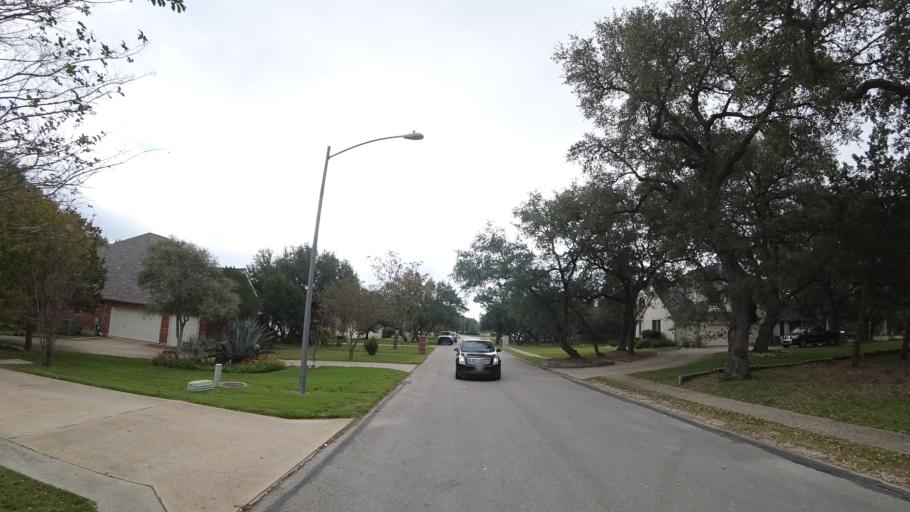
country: US
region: Texas
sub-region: Travis County
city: Barton Creek
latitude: 30.2577
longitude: -97.9086
